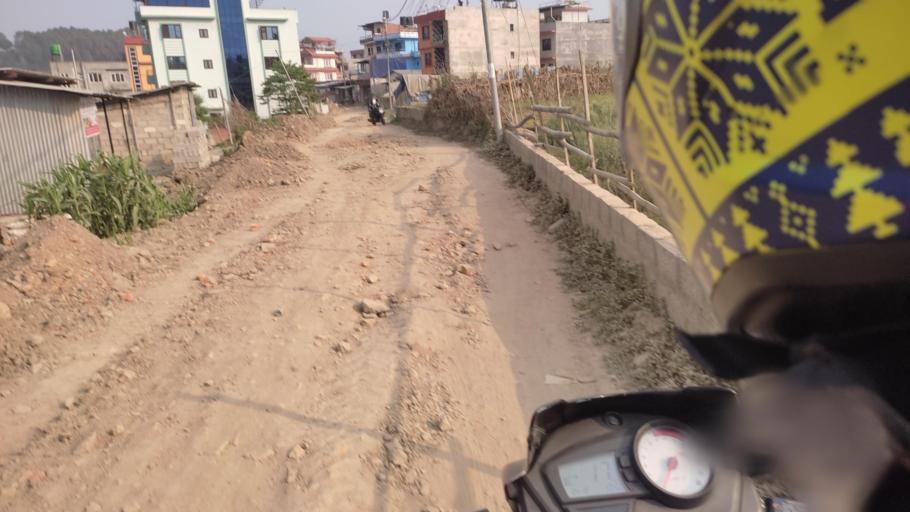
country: NP
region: Central Region
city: Kirtipur
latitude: 27.6597
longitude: 85.2874
